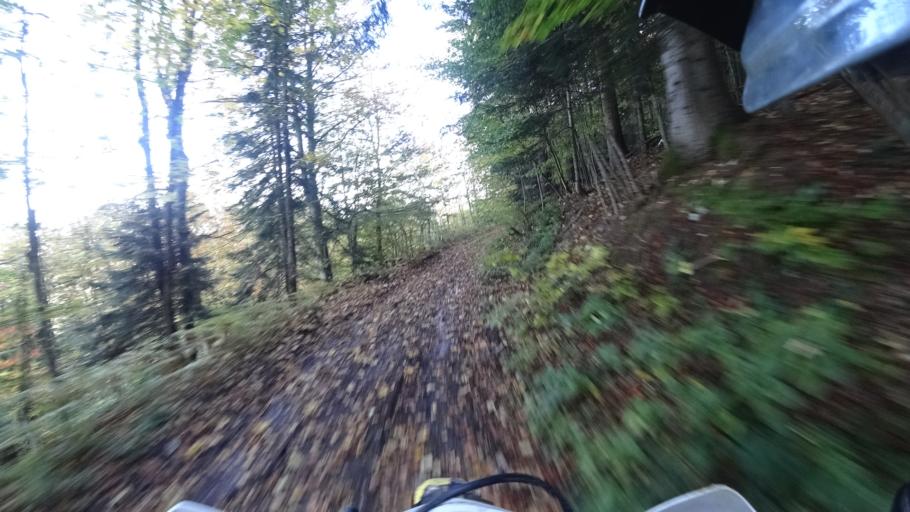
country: HR
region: Karlovacka
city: Plaski
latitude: 44.9648
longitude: 15.4394
